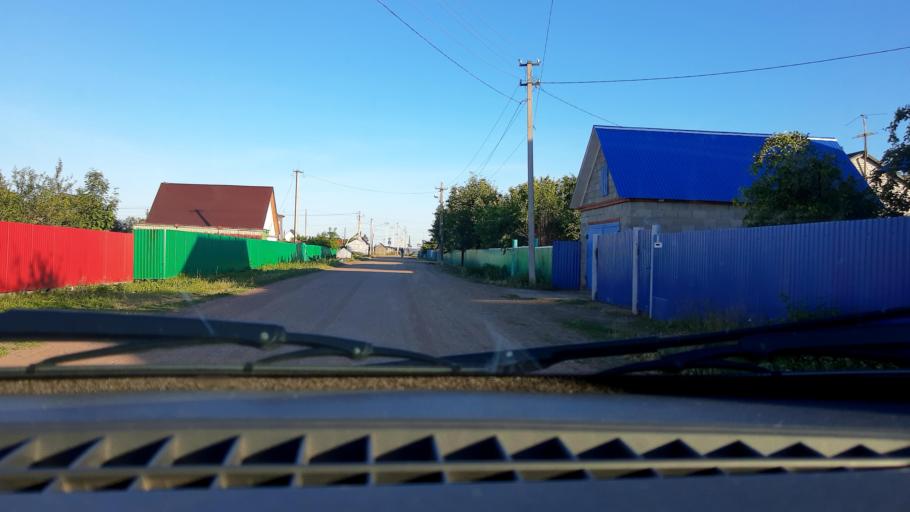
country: RU
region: Bashkortostan
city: Mikhaylovka
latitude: 54.8946
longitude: 55.9239
